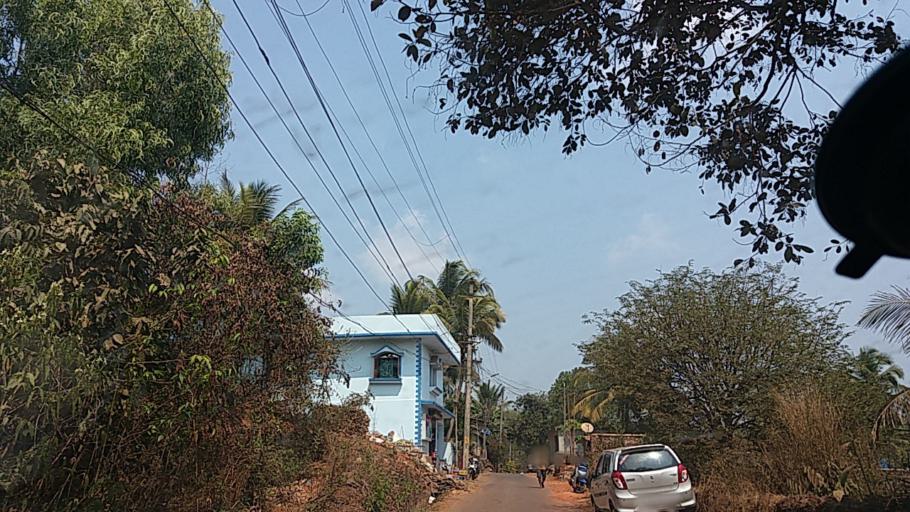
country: IN
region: Goa
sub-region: South Goa
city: Sancoale
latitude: 15.3709
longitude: 73.9150
